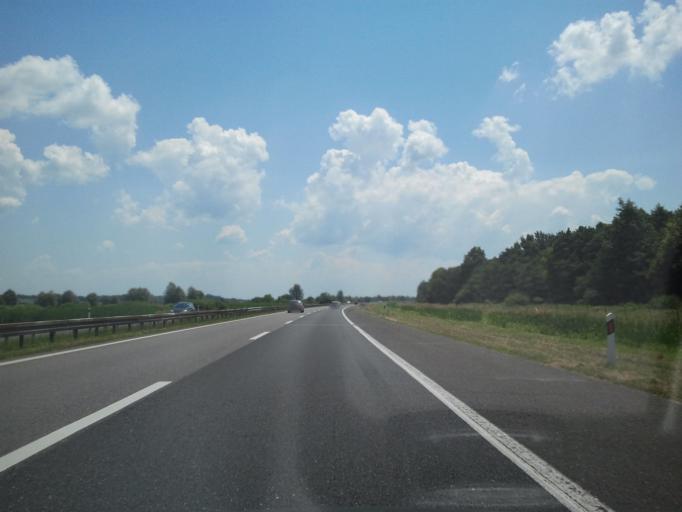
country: HR
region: Zagrebacka
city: Kriz
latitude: 45.6771
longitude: 16.4713
